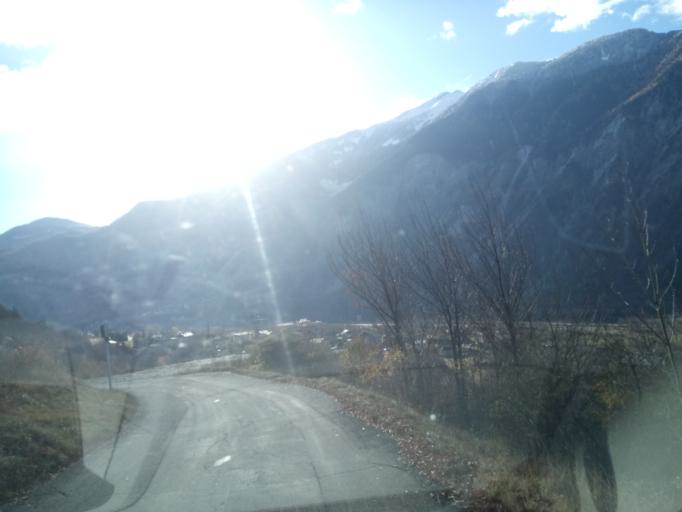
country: FR
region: Rhone-Alpes
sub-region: Departement de la Savoie
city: Villargondran
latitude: 45.2637
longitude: 6.3926
